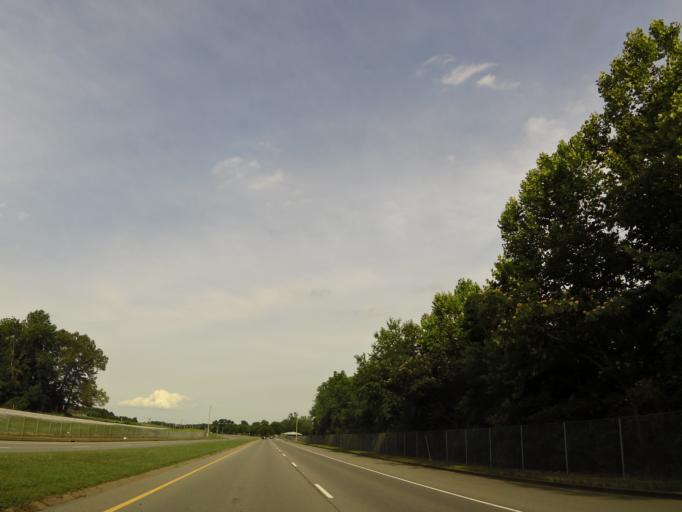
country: US
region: Tennessee
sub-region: Humphreys County
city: Waverly
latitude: 36.0848
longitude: -87.7813
